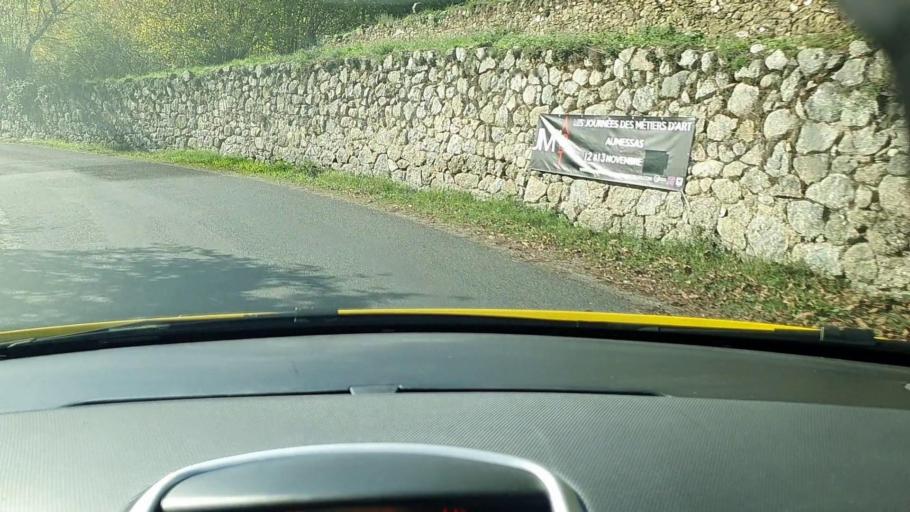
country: FR
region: Languedoc-Roussillon
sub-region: Departement du Gard
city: Le Vigan
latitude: 43.9881
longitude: 3.4975
